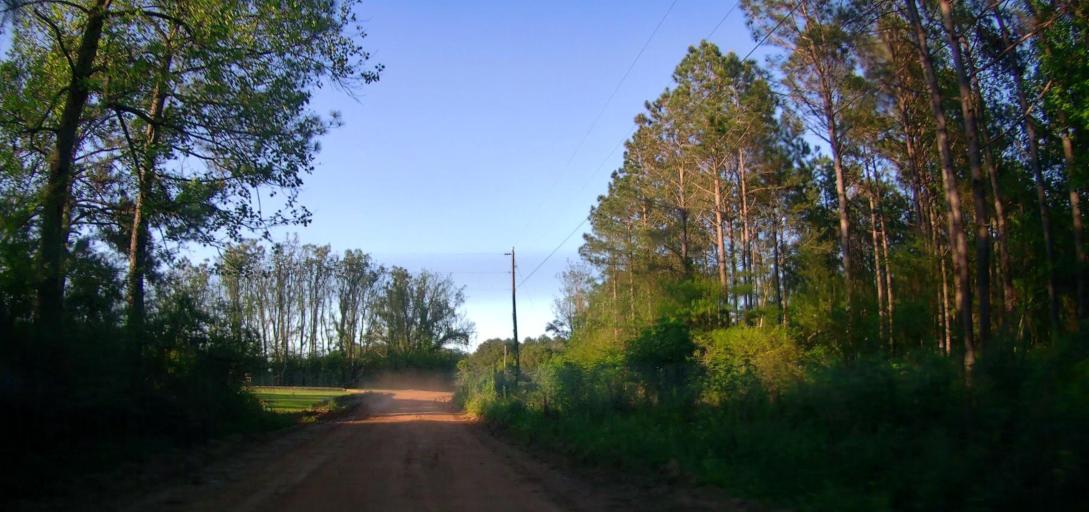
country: US
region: Georgia
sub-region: Irwin County
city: Ocilla
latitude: 31.6522
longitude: -83.2113
